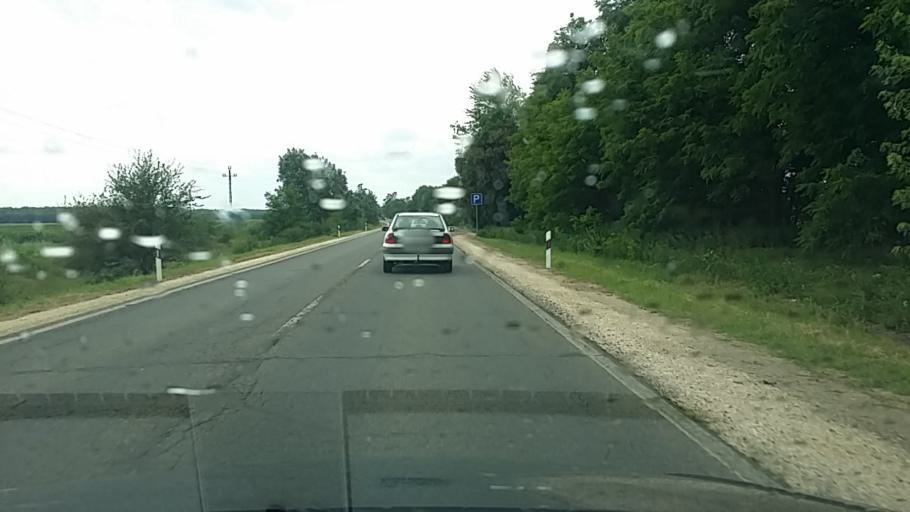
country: HU
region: Pest
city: Orkeny
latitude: 47.1372
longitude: 19.4090
